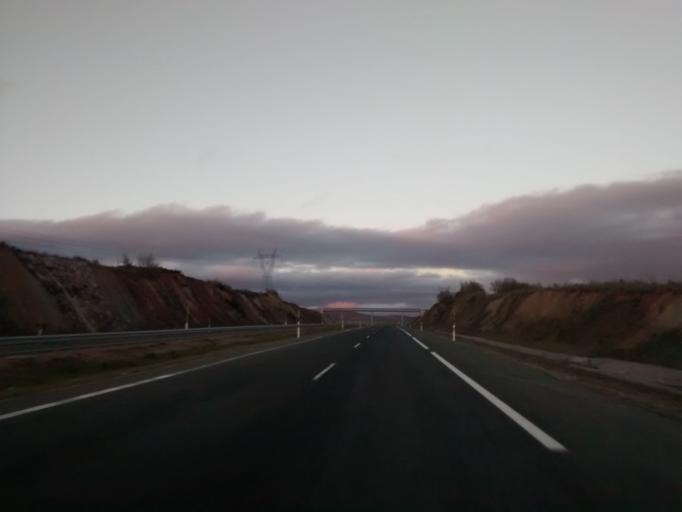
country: ES
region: Cantabria
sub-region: Provincia de Cantabria
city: Mataporquera
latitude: 42.8294
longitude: -4.2009
